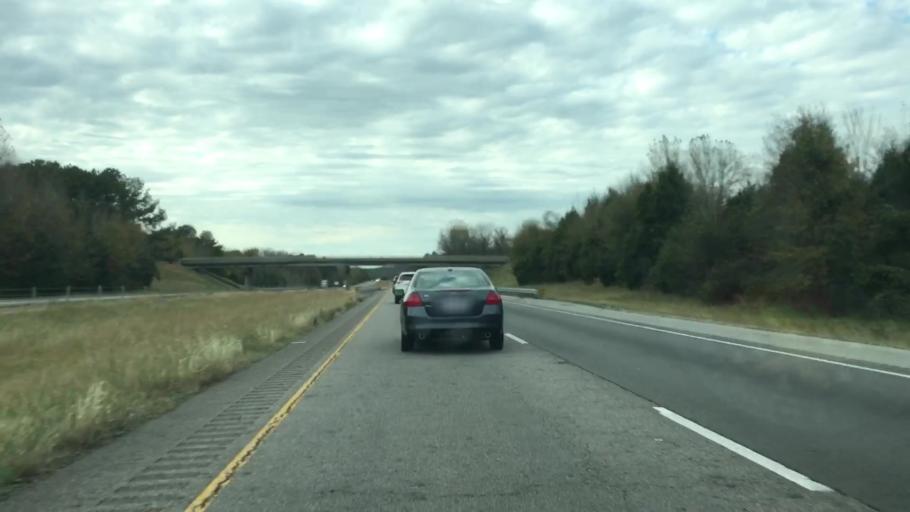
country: US
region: Arkansas
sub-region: Faulkner County
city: Conway
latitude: 35.1528
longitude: -92.5516
